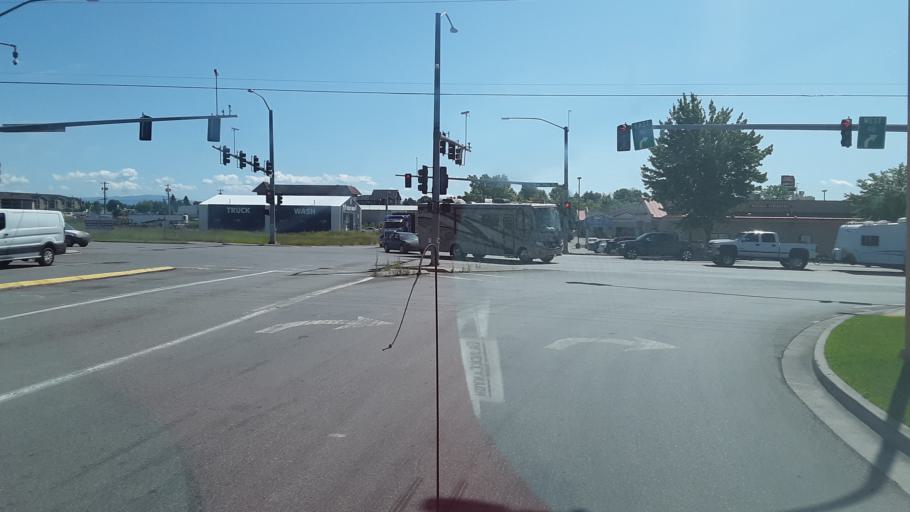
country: US
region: Idaho
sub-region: Kootenai County
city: Post Falls
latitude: 47.7118
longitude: -117.0024
